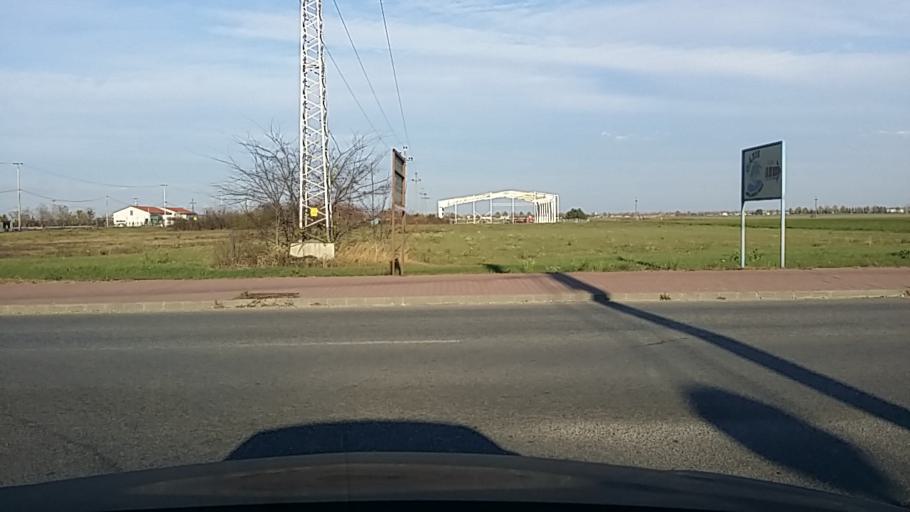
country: HU
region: Pest
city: Szigetszentmiklos
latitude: 47.3585
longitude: 19.0309
